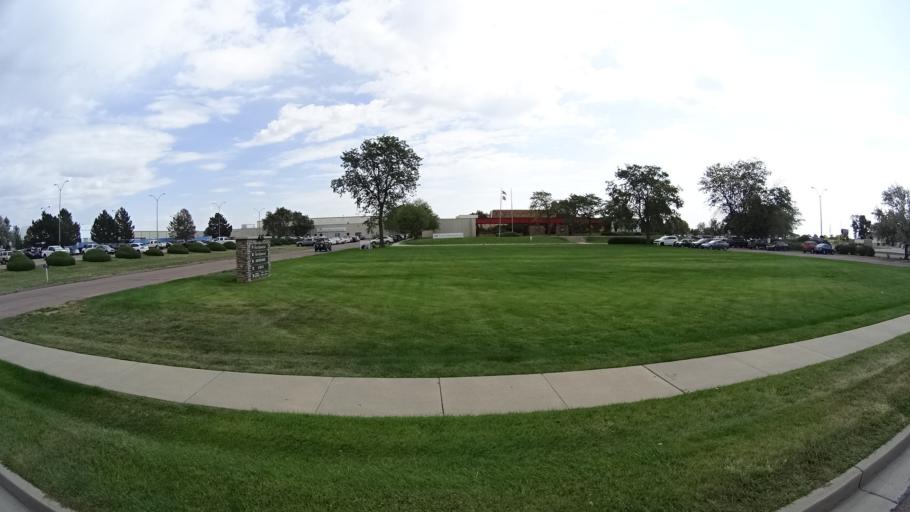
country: US
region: Colorado
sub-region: El Paso County
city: Cimarron Hills
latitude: 38.8419
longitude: -104.7388
